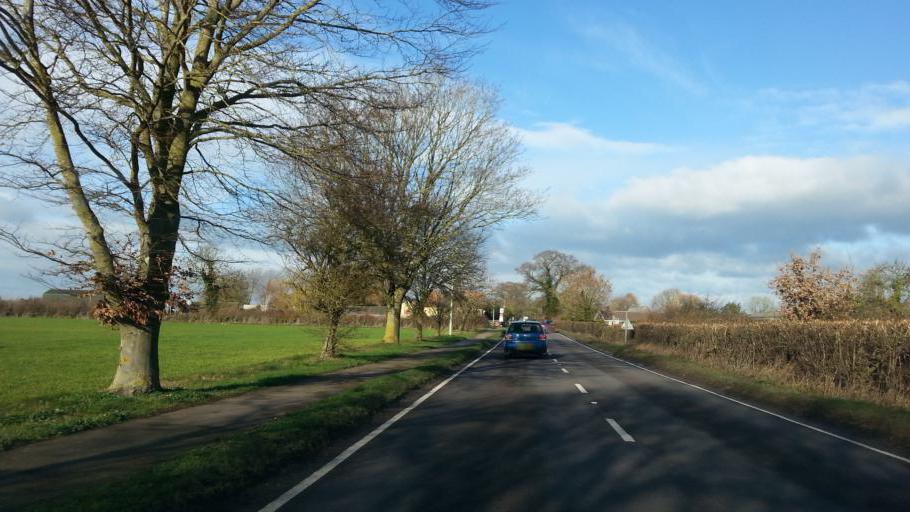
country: GB
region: England
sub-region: Suffolk
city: Halesworth
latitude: 52.3883
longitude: 1.5006
